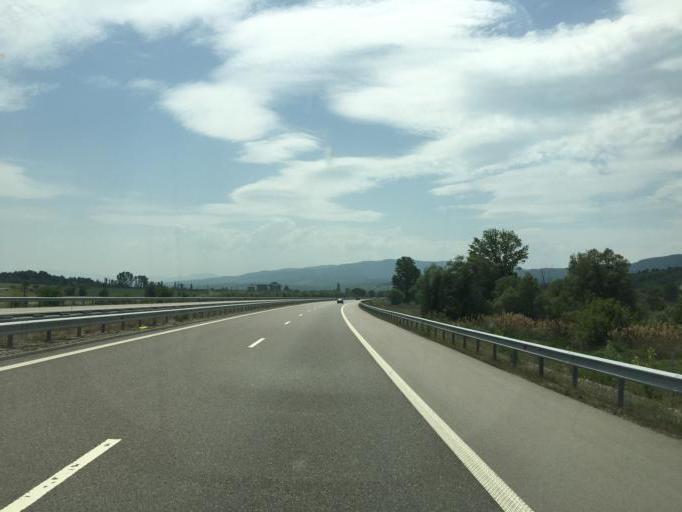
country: BG
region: Kyustendil
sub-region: Obshtina Boboshevo
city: Boboshevo
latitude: 42.1710
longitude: 23.0453
